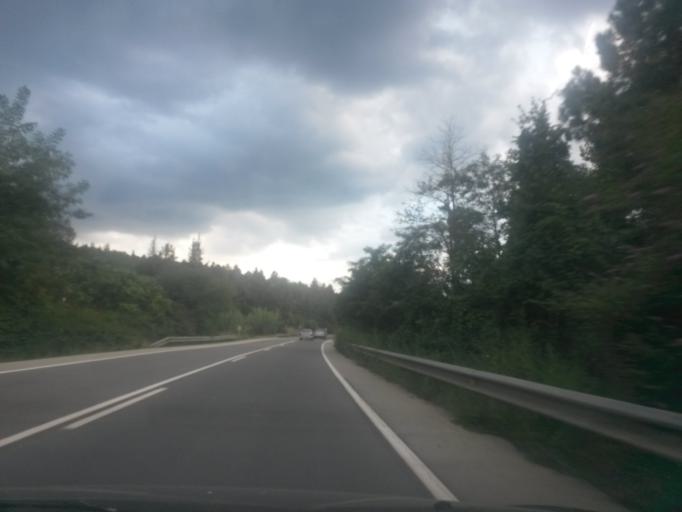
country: ES
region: Catalonia
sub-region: Provincia de Girona
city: Angles
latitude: 41.9459
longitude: 2.6420
